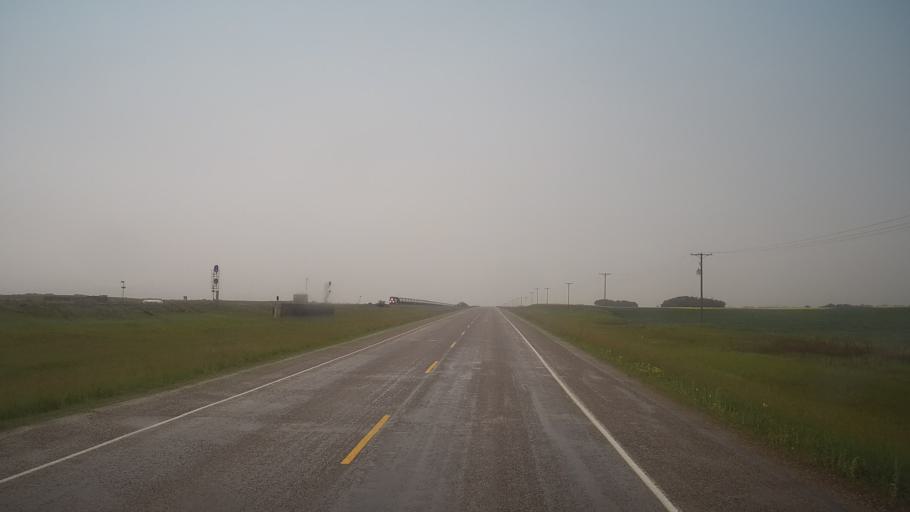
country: CA
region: Saskatchewan
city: Biggar
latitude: 52.1565
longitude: -108.2588
